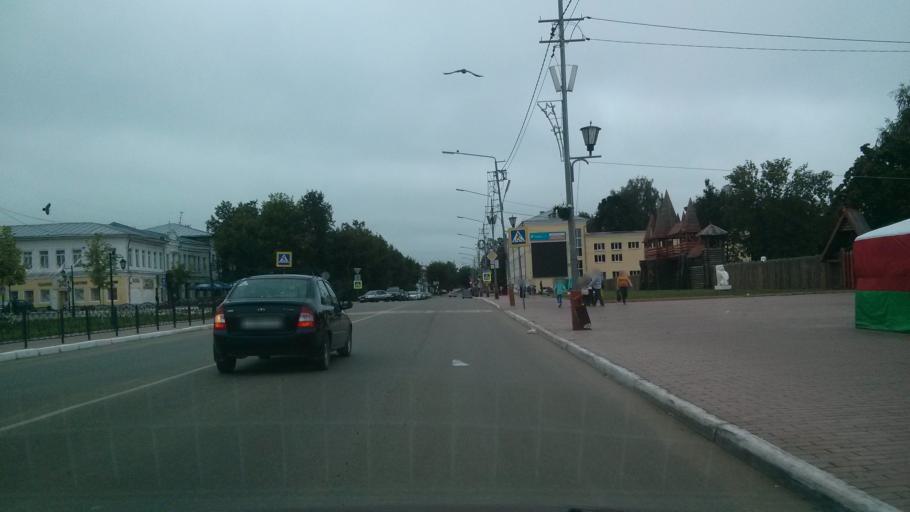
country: RU
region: Vladimir
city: Murom
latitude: 55.5785
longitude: 42.0530
